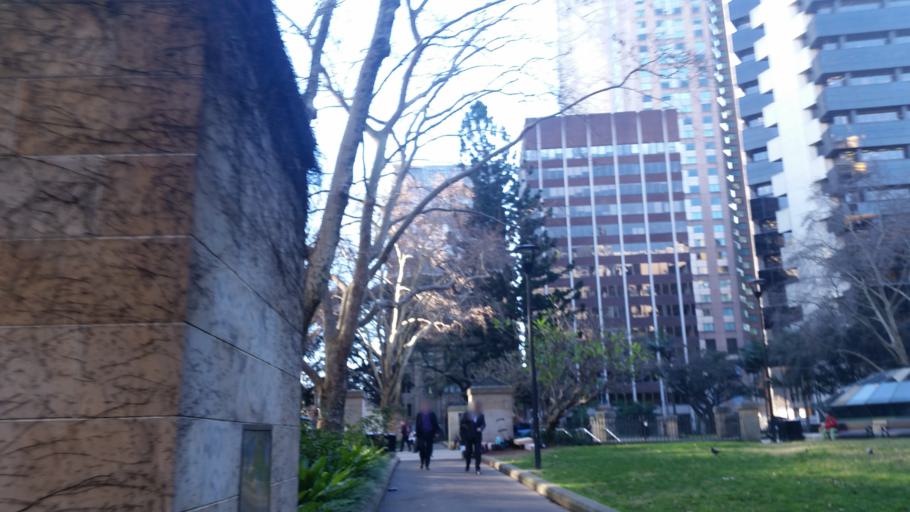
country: AU
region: New South Wales
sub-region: City of Sydney
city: Sydney
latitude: -33.8661
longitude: 151.2063
